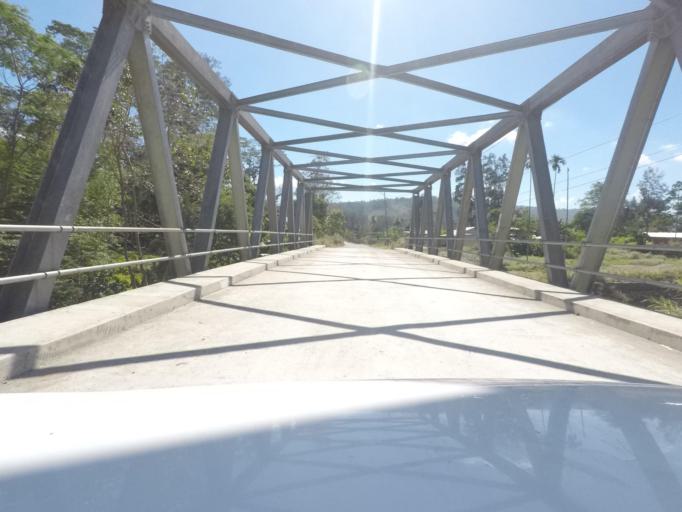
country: TL
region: Ermera
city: Gleno
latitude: -8.7170
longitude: 125.4309
